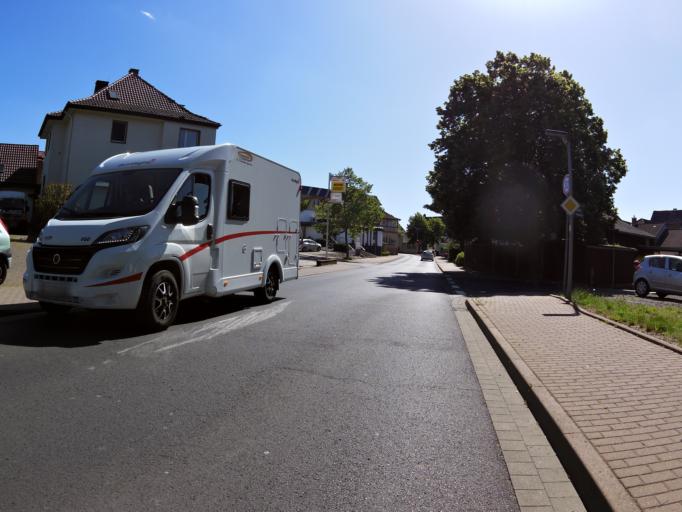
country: DE
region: Hesse
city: Philippsthal
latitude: 50.8402
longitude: 9.9980
